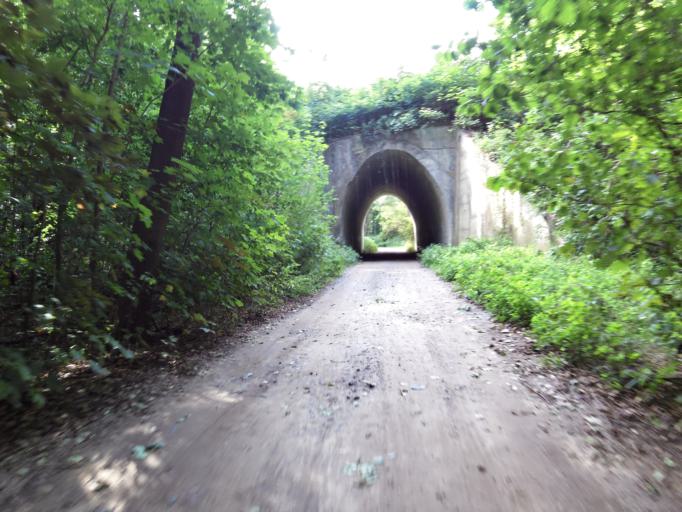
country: DE
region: Mecklenburg-Vorpommern
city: Seebad Bansin
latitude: 53.9753
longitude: 14.1067
